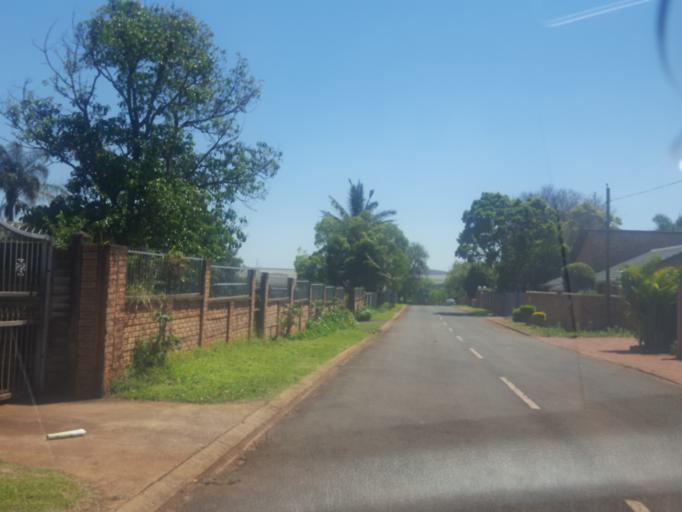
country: ZA
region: KwaZulu-Natal
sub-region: uThungulu District Municipality
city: Empangeni
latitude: -28.7469
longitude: 31.9069
